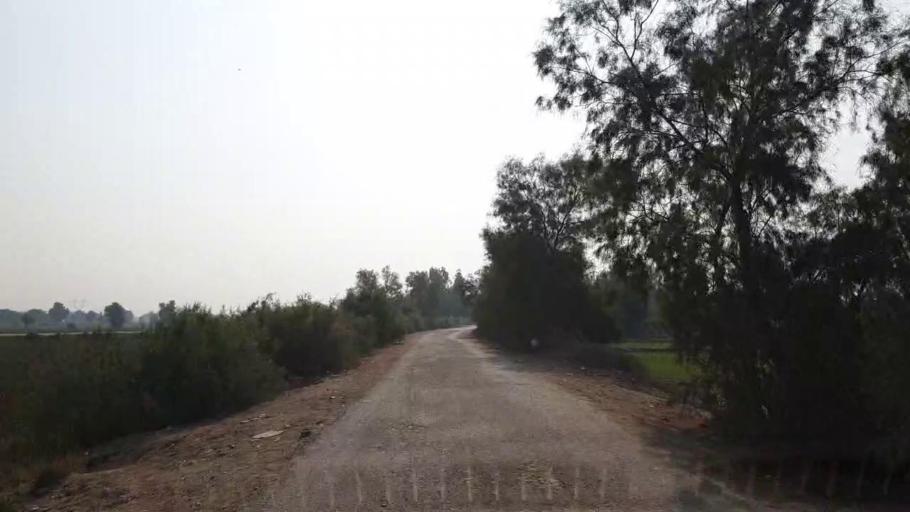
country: PK
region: Sindh
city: Sehwan
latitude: 26.4678
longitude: 67.7771
